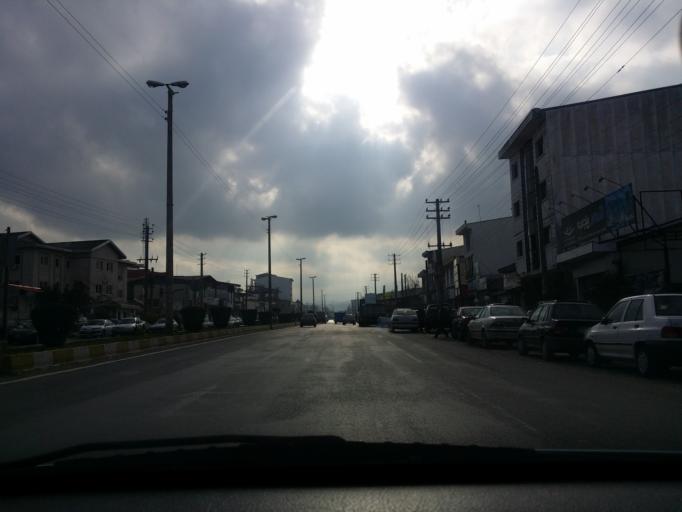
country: IR
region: Mazandaran
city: Chalus
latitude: 36.6753
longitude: 51.4049
